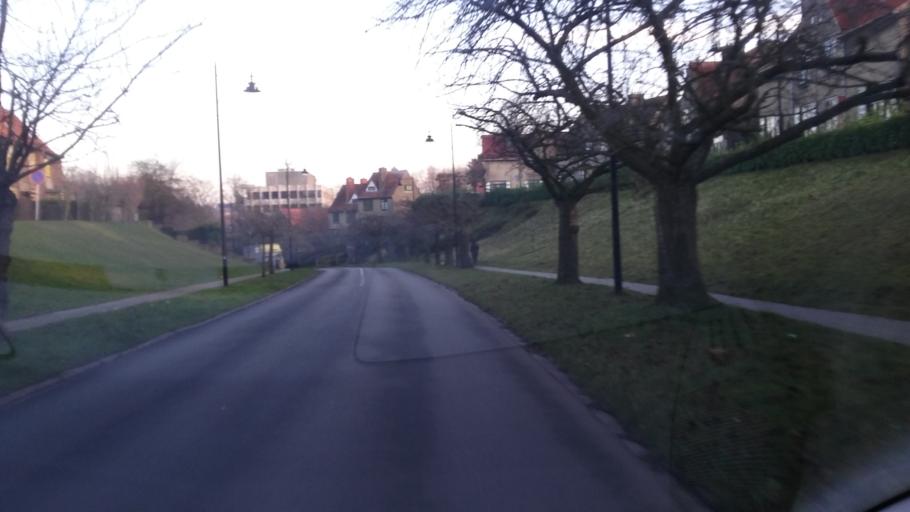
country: BE
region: Flanders
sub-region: Provincie Vlaams-Brabant
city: Hoeilaart
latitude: 50.8074
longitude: 4.4216
